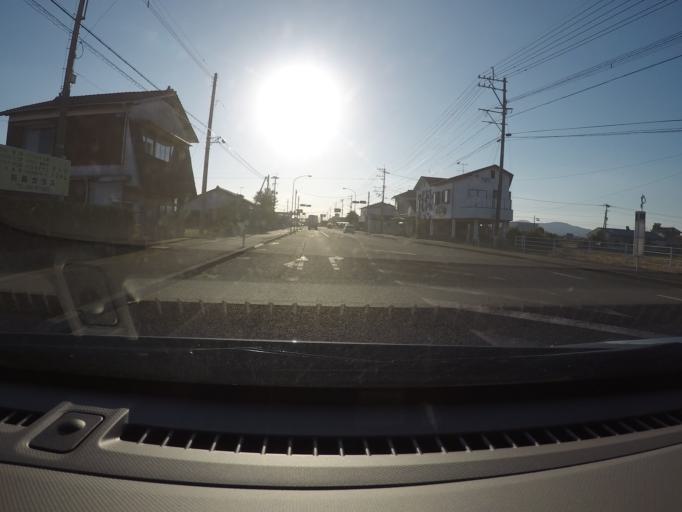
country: JP
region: Kagoshima
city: Izumi
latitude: 32.1130
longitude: 130.3323
